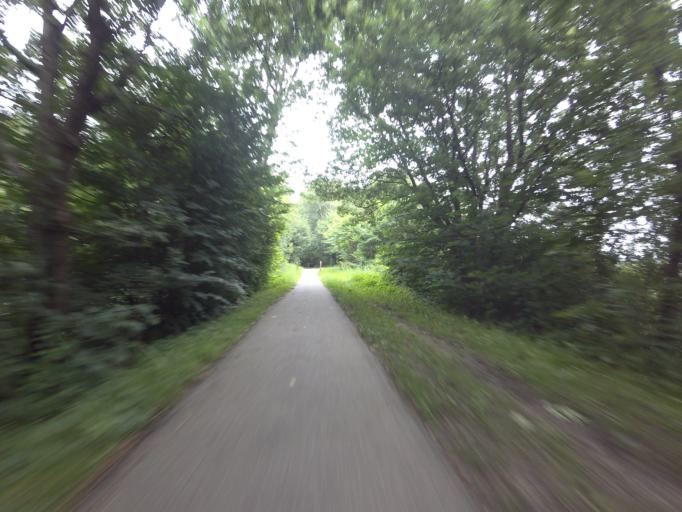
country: DK
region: Central Jutland
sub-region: Horsens Kommune
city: Braedstrup
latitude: 56.0217
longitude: 9.5299
